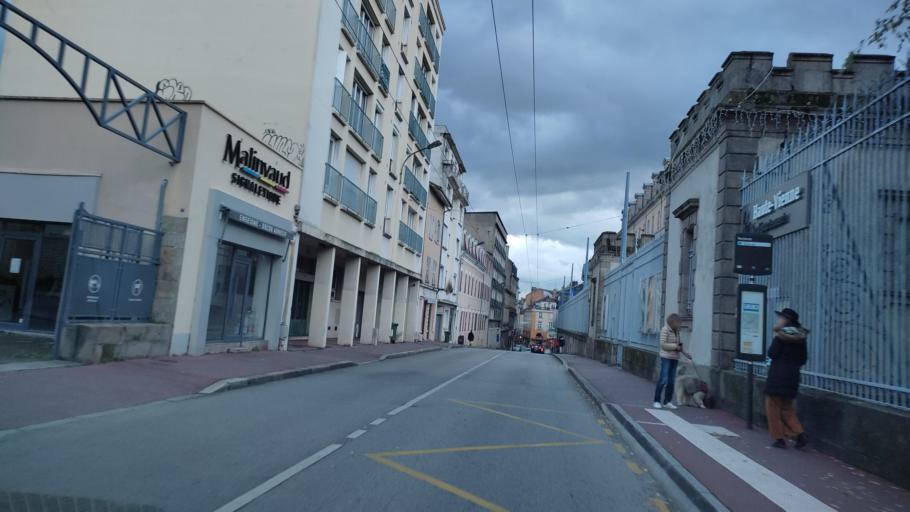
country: FR
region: Limousin
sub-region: Departement de la Haute-Vienne
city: Limoges
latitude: 45.8348
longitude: 1.2558
